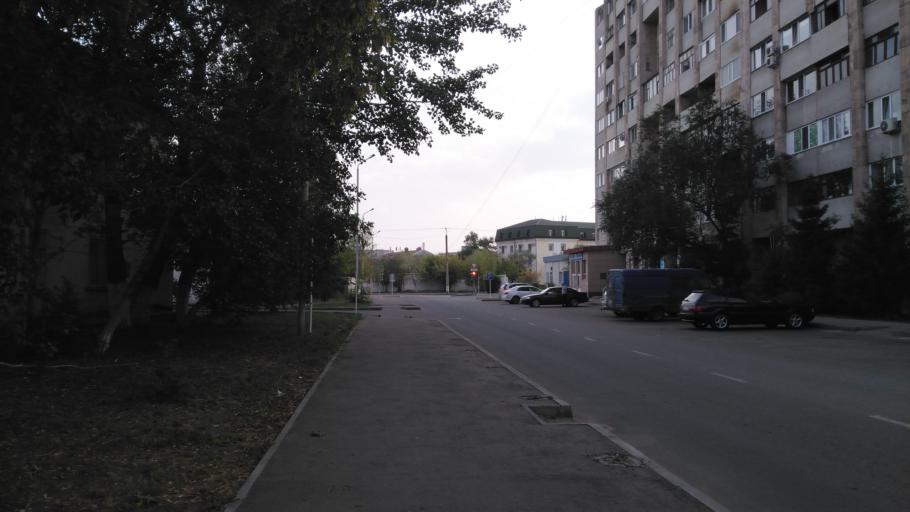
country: KZ
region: Pavlodar
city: Pavlodar
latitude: 52.2999
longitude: 76.9469
